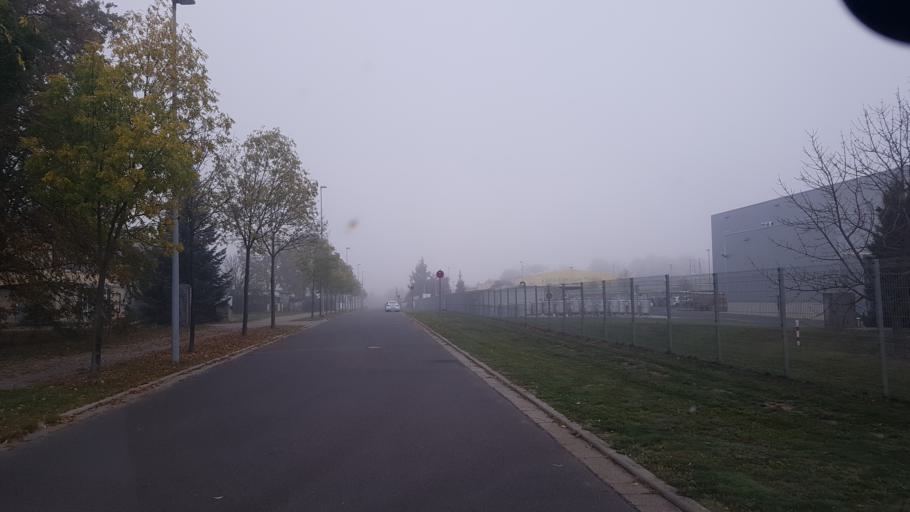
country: DE
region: Brandenburg
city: Elsterwerda
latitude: 51.4623
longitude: 13.5418
